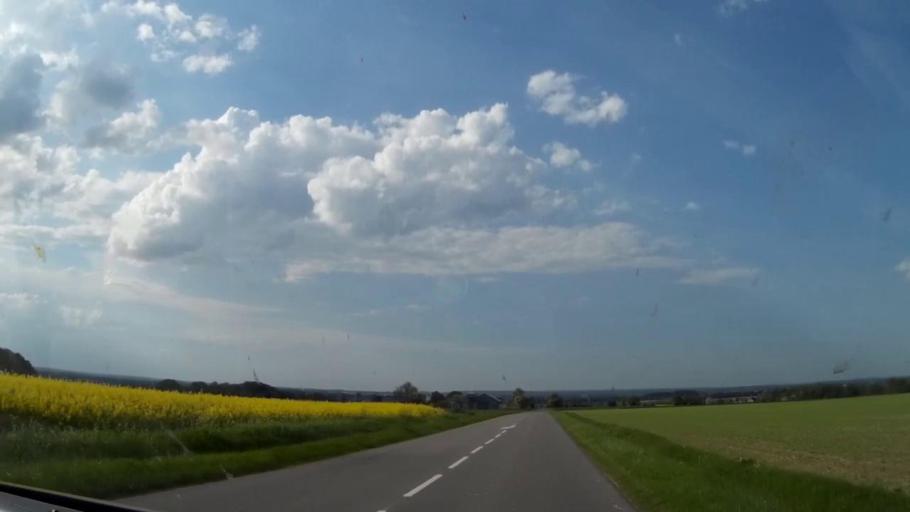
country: FR
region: Centre
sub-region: Departement du Loir-et-Cher
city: Mondoubleau
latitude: 47.9601
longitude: 0.9299
